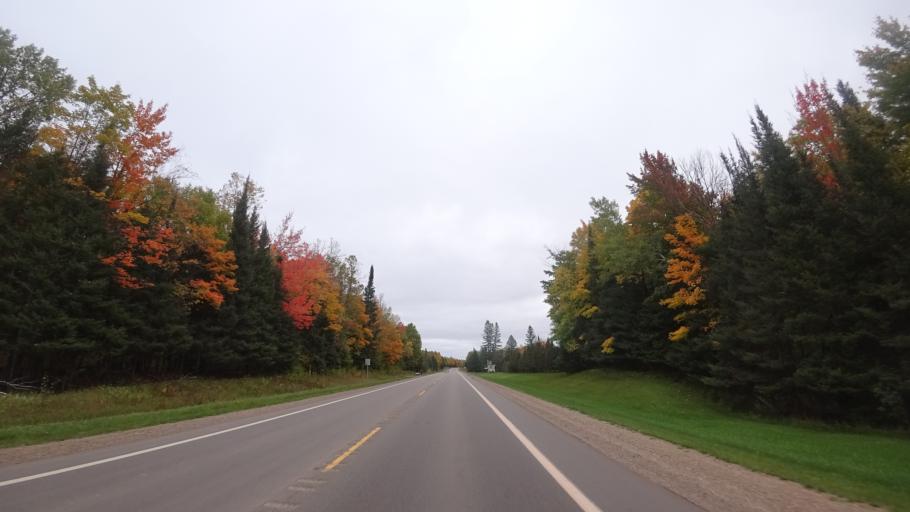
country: US
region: Michigan
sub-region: Iron County
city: Crystal Falls
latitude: 46.1611
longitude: -88.0787
